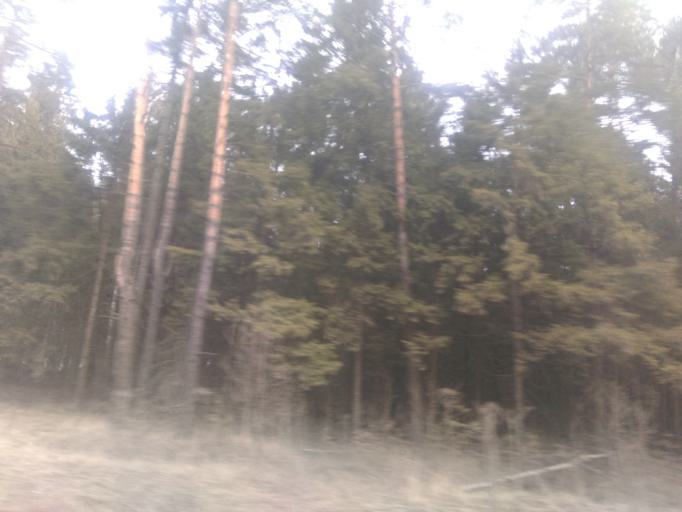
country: RU
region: Moskovskaya
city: Tuchkovo
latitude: 55.5661
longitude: 36.5235
